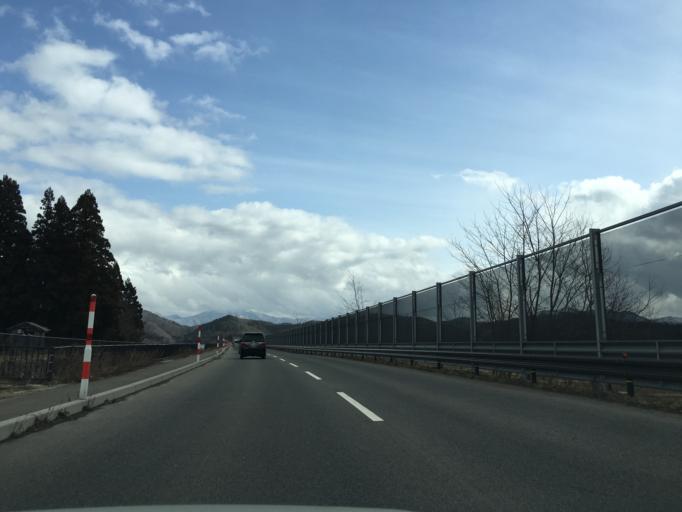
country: JP
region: Akita
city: Hanawa
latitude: 40.2316
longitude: 140.7030
